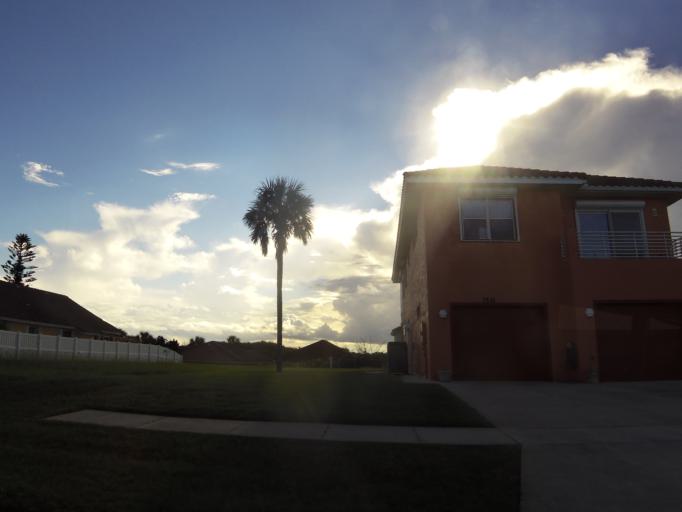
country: US
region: Florida
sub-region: Flagler County
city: Flagler Beach
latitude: 29.4955
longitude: -81.1351
